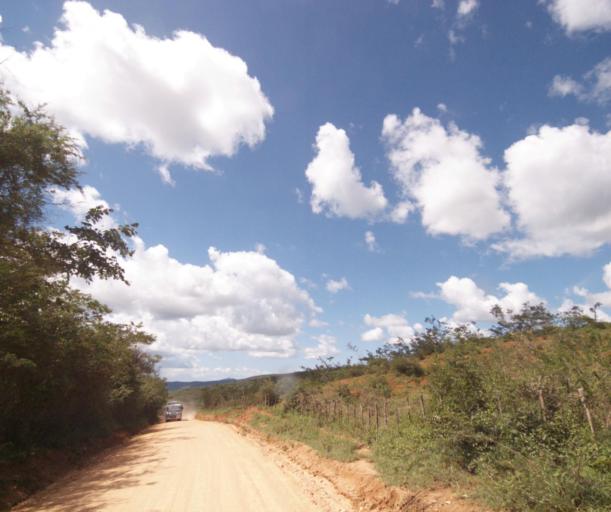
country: BR
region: Bahia
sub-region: Pocoes
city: Pocoes
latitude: -14.2982
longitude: -40.6795
